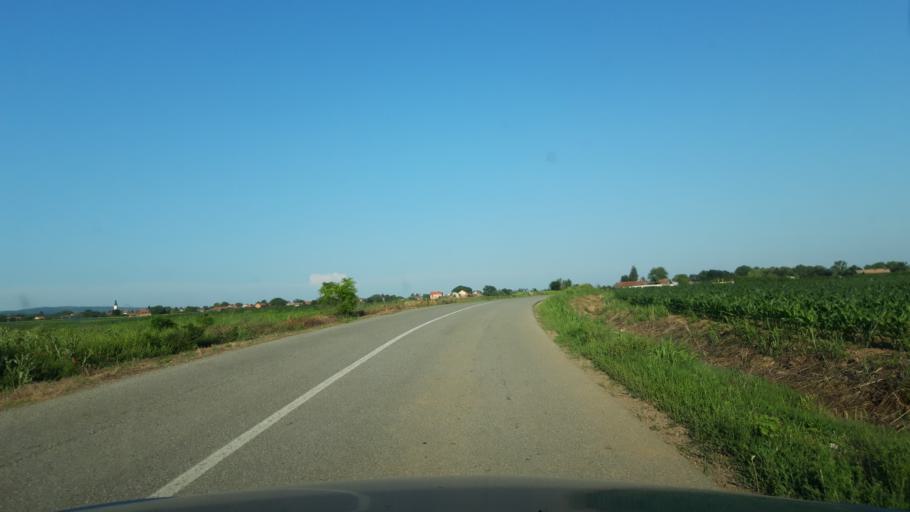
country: HR
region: Vukovarsko-Srijemska
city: Ilok
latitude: 45.1065
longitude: 19.4913
